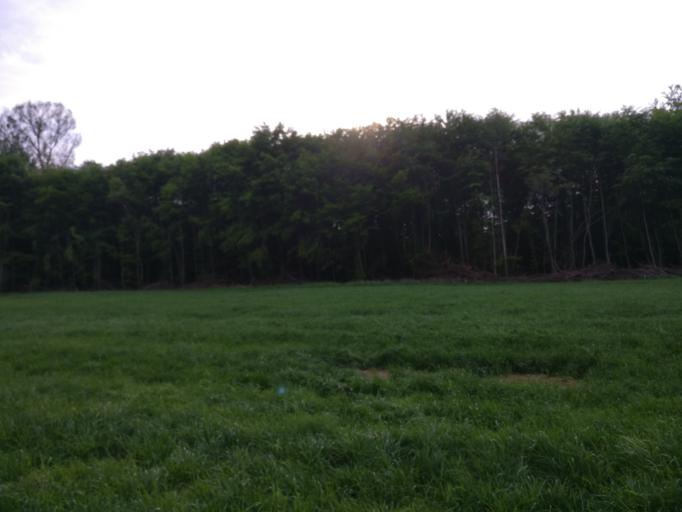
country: DE
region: Rheinland-Pfalz
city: Kaltenholzhausen
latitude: 50.2919
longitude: 8.1618
